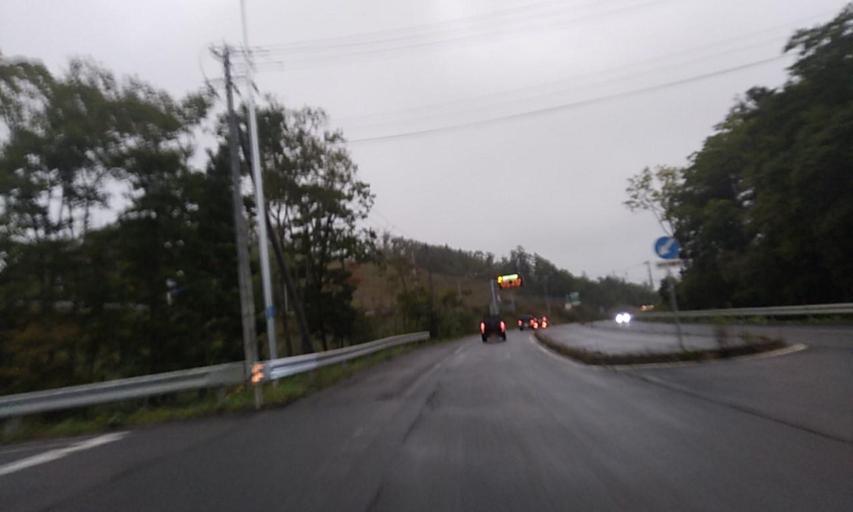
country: JP
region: Hokkaido
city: Kushiro
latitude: 43.0038
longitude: 144.5020
